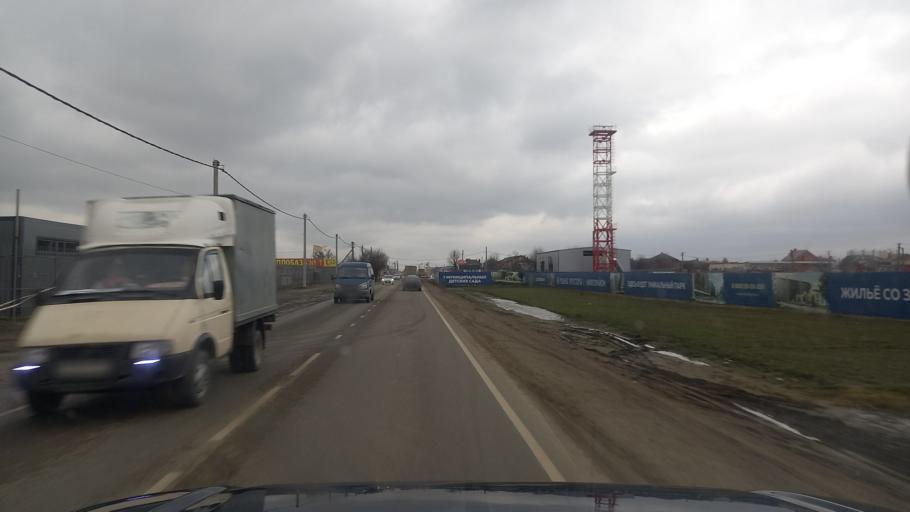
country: RU
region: Krasnodarskiy
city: Pashkovskiy
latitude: 45.0591
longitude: 39.1447
